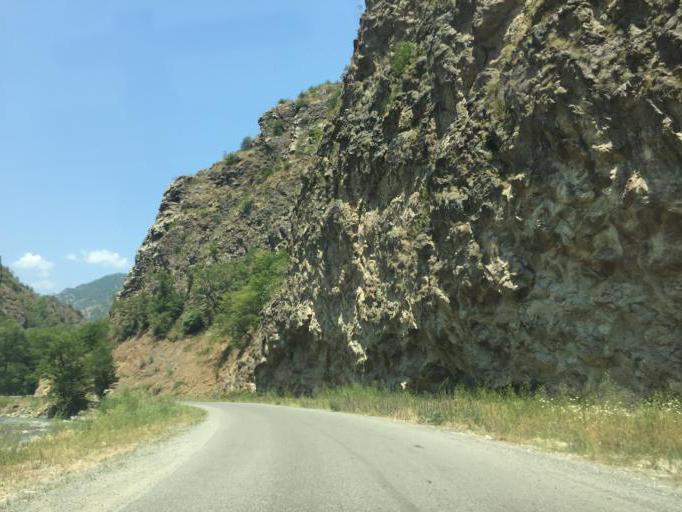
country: AZ
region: Kalbacar Rayonu
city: Kerbakhiar
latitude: 40.1244
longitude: 46.4043
